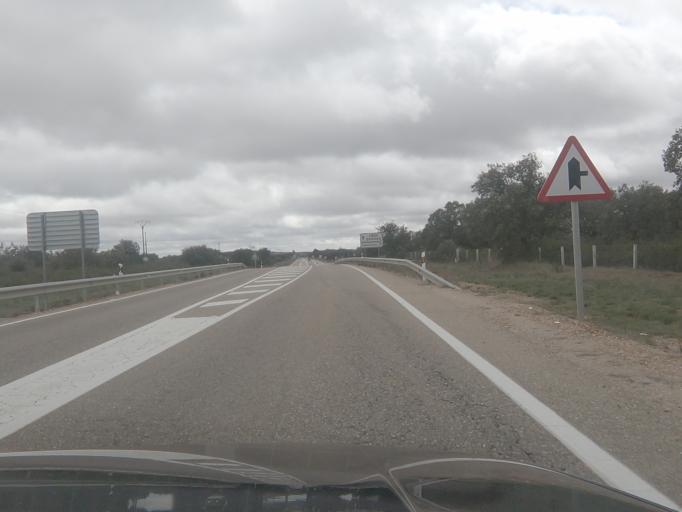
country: ES
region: Castille and Leon
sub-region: Provincia de Zamora
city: San Cebrian de Castro
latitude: 41.7186
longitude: -5.8101
